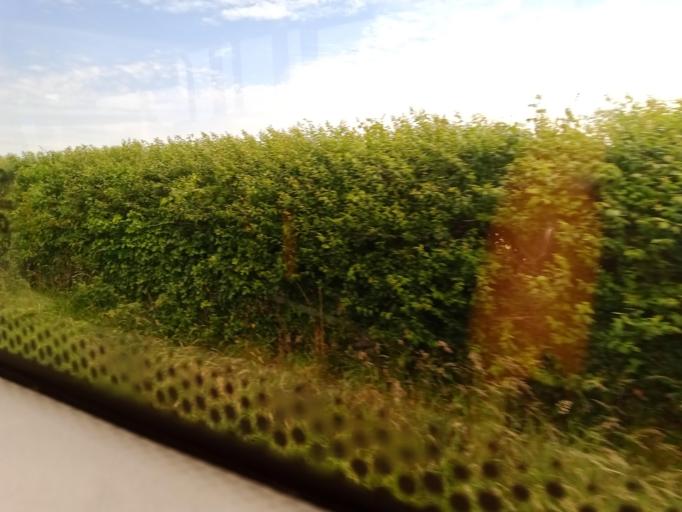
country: GB
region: Wales
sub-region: Anglesey
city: Llangoed
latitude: 53.2960
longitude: -4.0697
